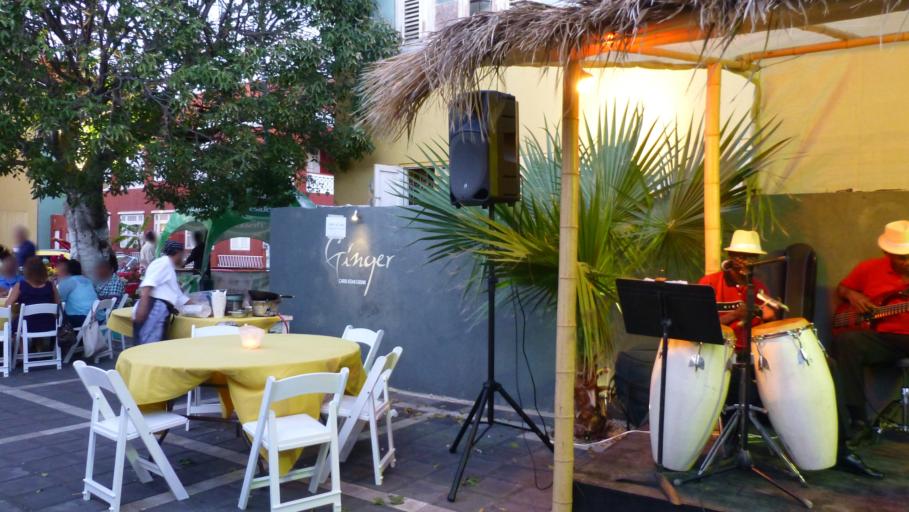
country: CW
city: Willemstad
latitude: 12.1032
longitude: -68.9286
